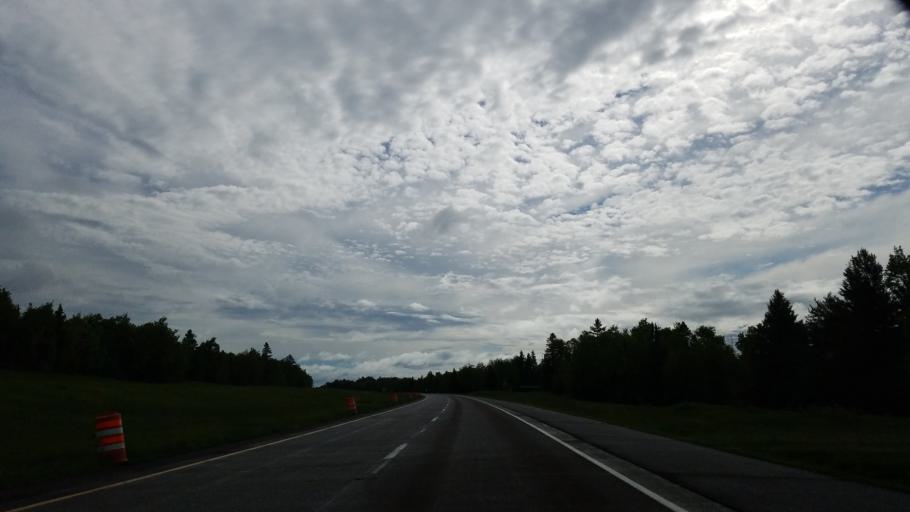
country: US
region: Minnesota
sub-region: Lake County
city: Two Harbors
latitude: 46.9303
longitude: -91.8329
